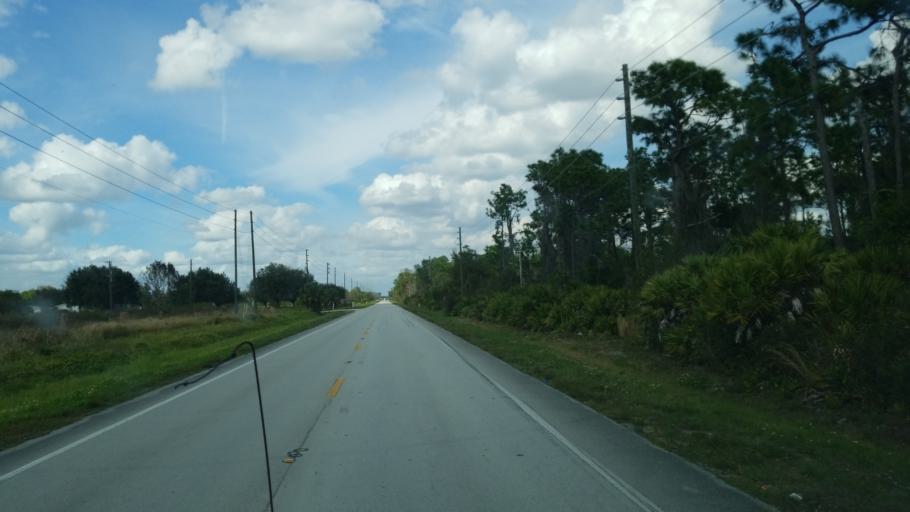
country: US
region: Florida
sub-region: Osceola County
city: Saint Cloud
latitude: 28.1142
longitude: -81.0763
